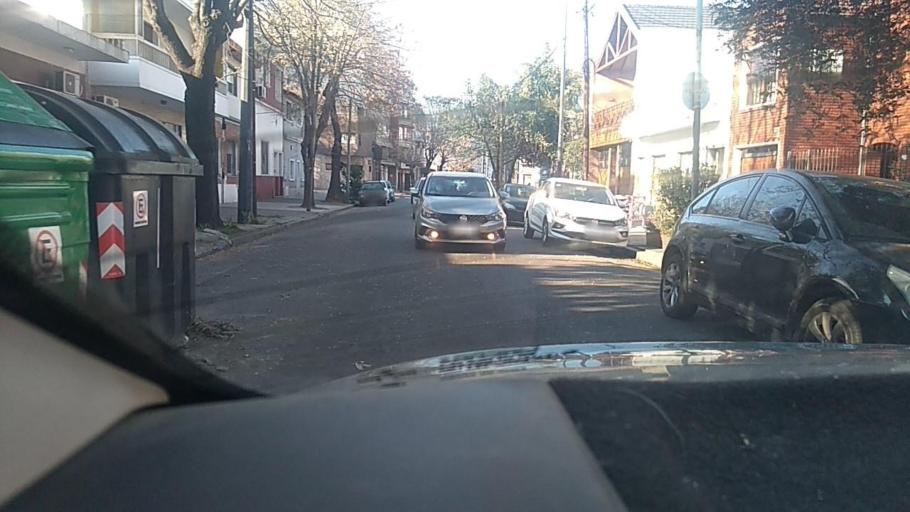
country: AR
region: Buenos Aires F.D.
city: Villa Santa Rita
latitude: -34.6134
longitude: -58.5187
